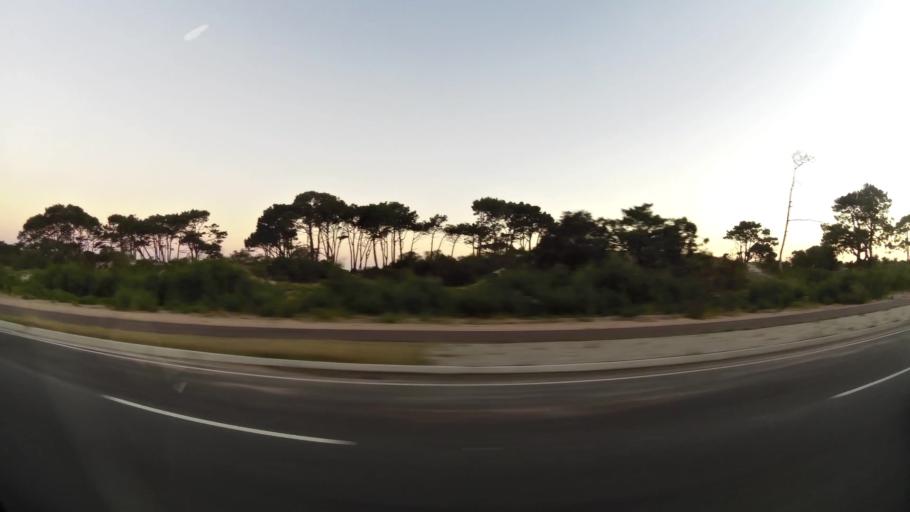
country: UY
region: Canelones
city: Barra de Carrasco
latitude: -34.8295
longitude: -55.9445
